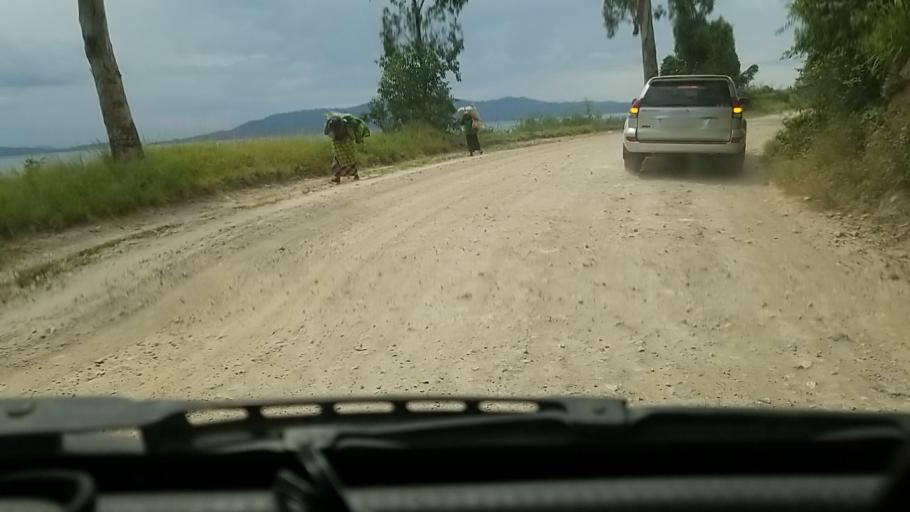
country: CD
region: Nord Kivu
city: Sake
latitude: -1.5931
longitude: 29.0404
